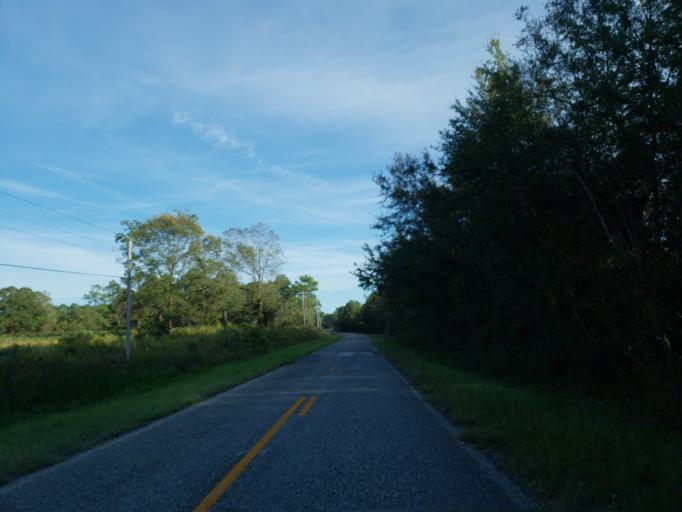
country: US
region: Georgia
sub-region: Crisp County
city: Cordele
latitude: 32.0203
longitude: -83.7370
